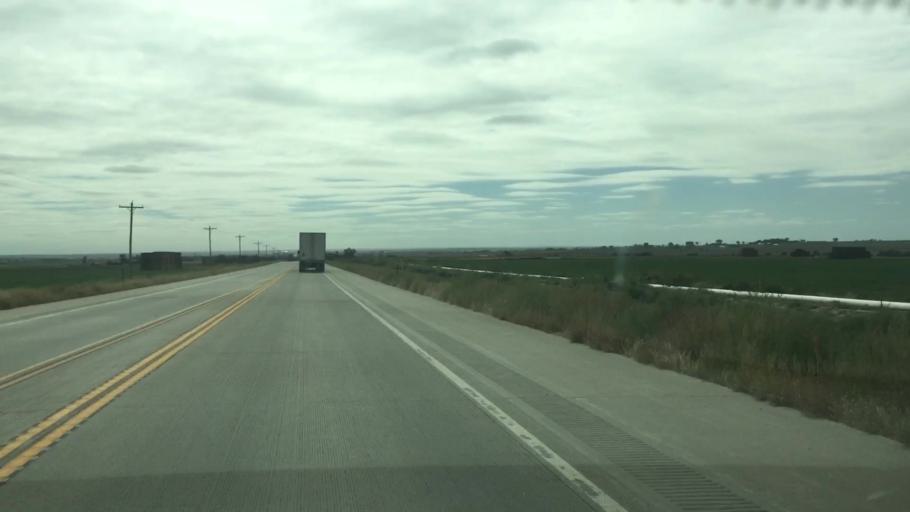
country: US
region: Colorado
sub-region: Prowers County
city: Lamar
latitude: 38.1969
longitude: -102.7242
